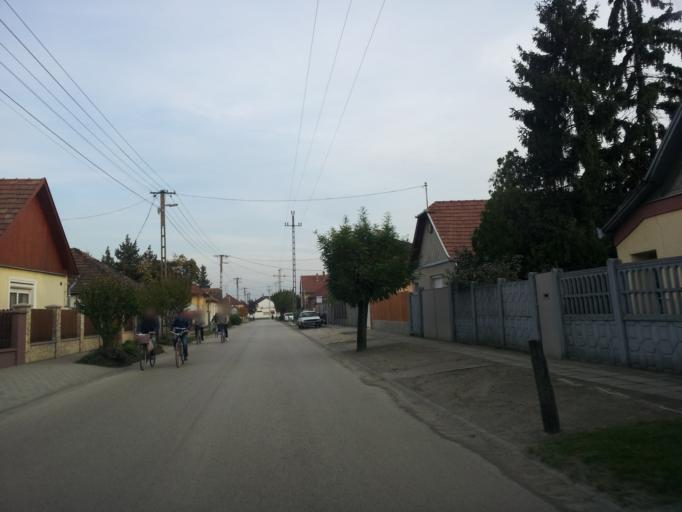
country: HU
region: Pest
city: Nagykata
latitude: 47.4116
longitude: 19.7434
